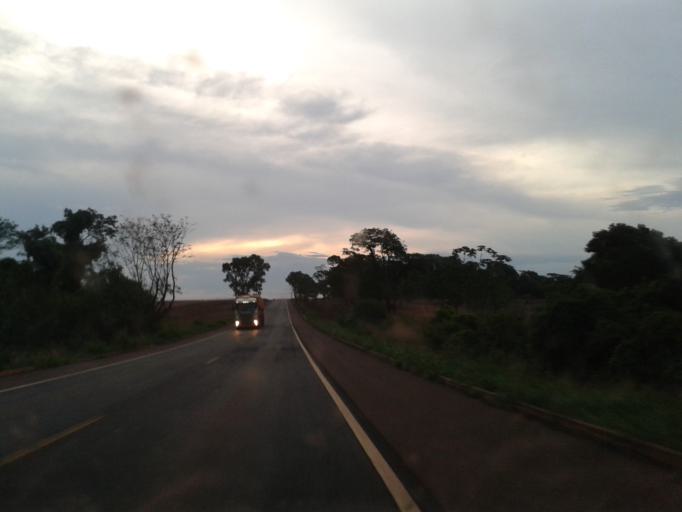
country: BR
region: Goias
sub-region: Santa Helena De Goias
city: Santa Helena de Goias
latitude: -17.8833
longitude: -50.6918
